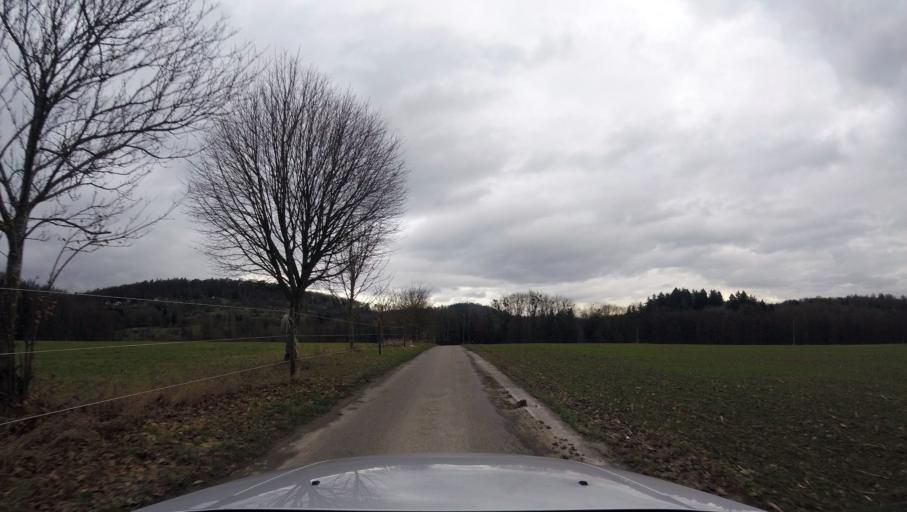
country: DE
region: Baden-Wuerttemberg
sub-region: Regierungsbezirk Stuttgart
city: Aspach
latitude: 48.9771
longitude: 9.4171
